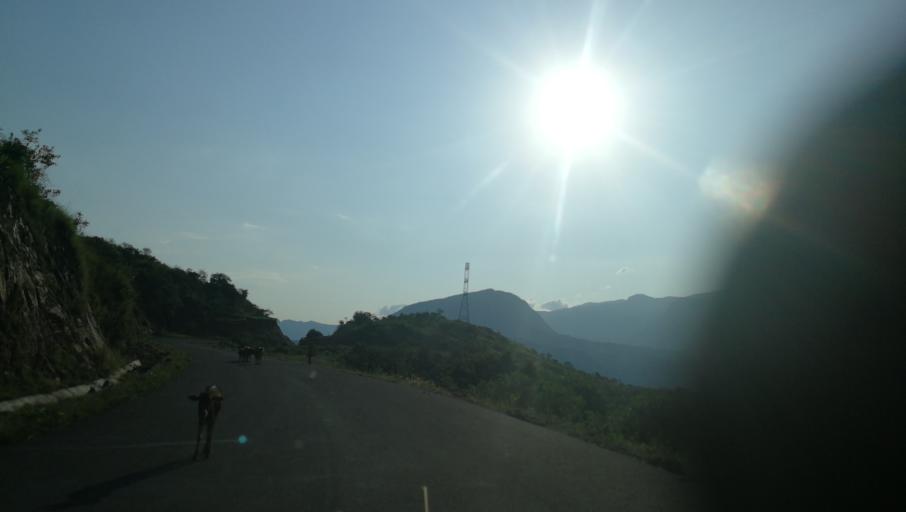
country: ET
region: Southern Nations, Nationalities, and People's Region
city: Areka
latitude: 6.8317
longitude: 37.3114
